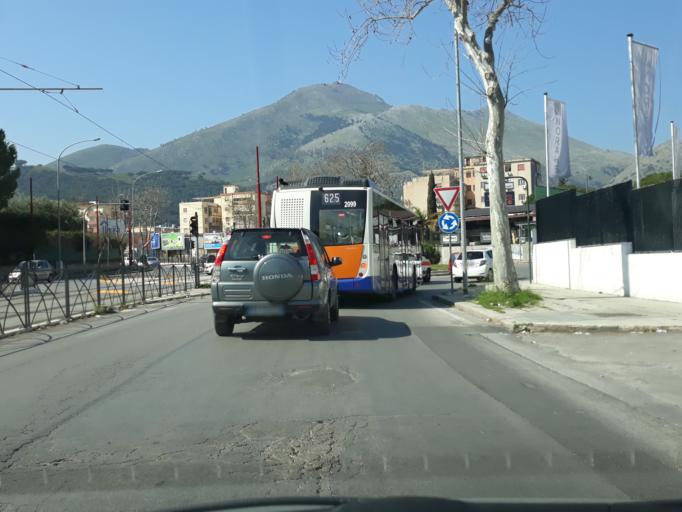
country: IT
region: Sicily
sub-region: Palermo
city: Palermo
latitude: 38.1311
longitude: 13.3044
